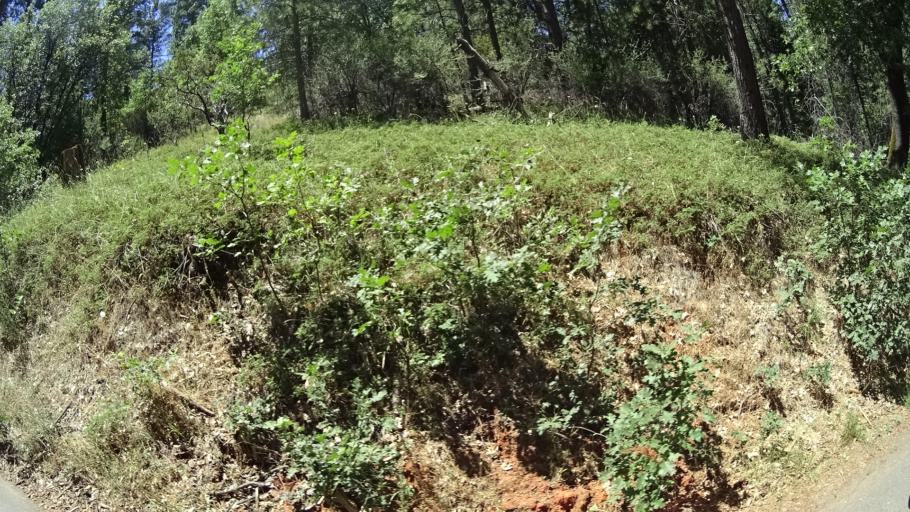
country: US
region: California
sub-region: Calaveras County
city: Arnold
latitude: 38.2487
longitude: -120.4271
